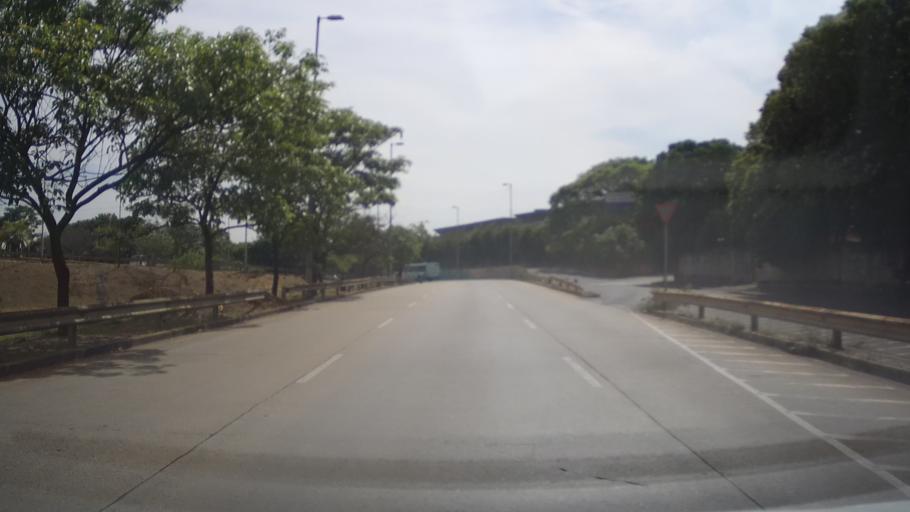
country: BR
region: Minas Gerais
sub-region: Belo Horizonte
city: Belo Horizonte
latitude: -19.9306
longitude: -43.9926
